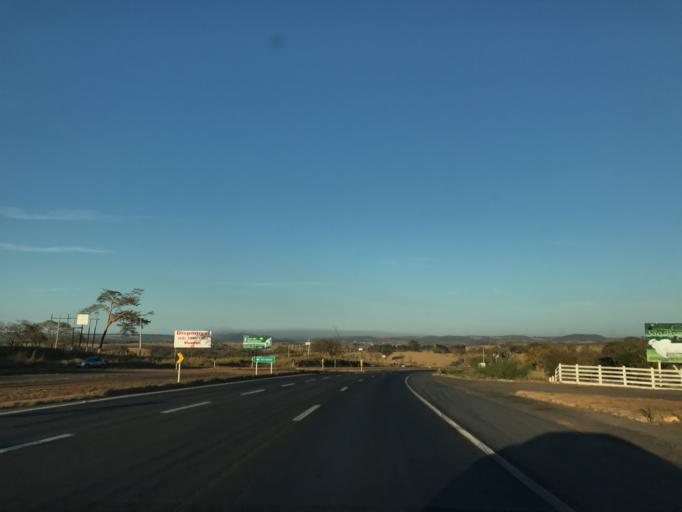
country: BR
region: Goias
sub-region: Goianapolis
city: Goianapolis
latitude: -16.4472
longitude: -49.0222
